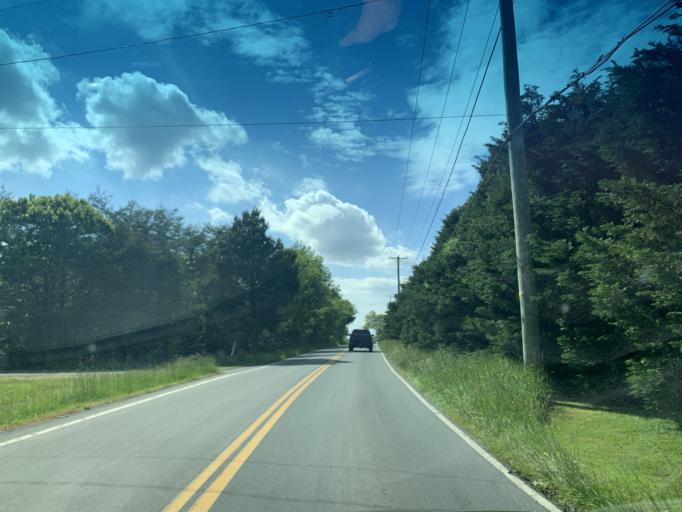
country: US
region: Maryland
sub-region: Cecil County
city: Rising Sun
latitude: 39.7133
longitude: -76.1534
